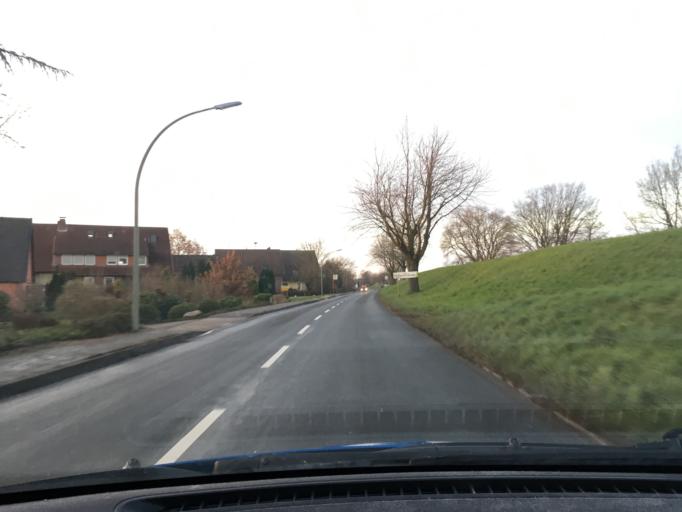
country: DE
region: Lower Saxony
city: Neu Wulmstorf
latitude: 53.5106
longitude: 9.8306
